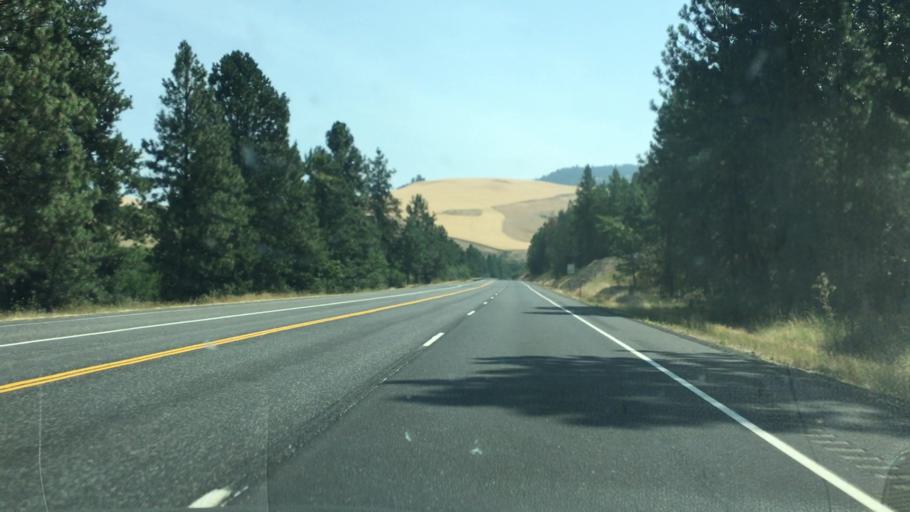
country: US
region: Idaho
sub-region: Nez Perce County
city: Lapwai
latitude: 46.3725
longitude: -116.6643
